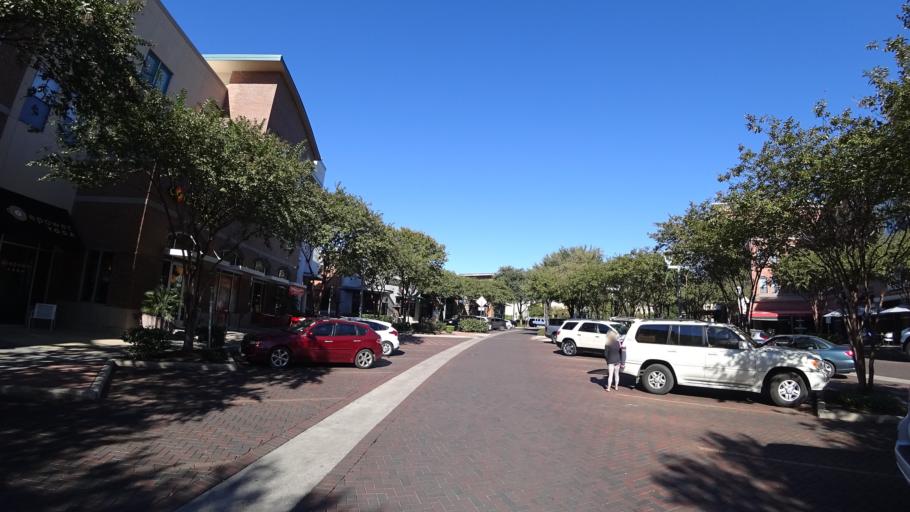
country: US
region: Texas
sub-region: Travis County
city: Austin
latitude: 30.3153
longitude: -97.7336
